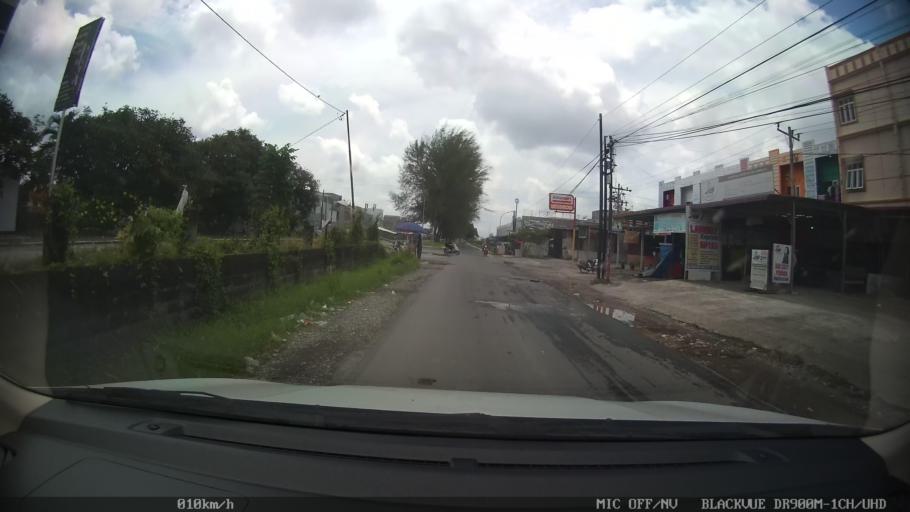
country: ID
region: North Sumatra
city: Medan
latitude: 3.6141
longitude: 98.7292
